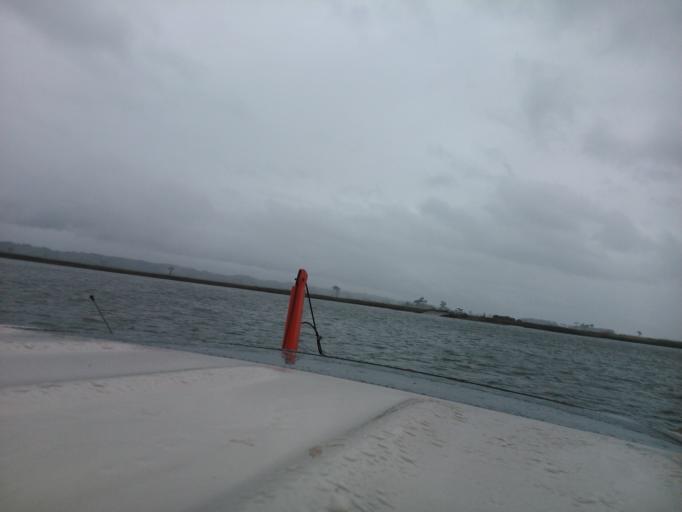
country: CL
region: Araucania
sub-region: Provincia de Cautin
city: Carahue
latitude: -38.7477
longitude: -73.4083
